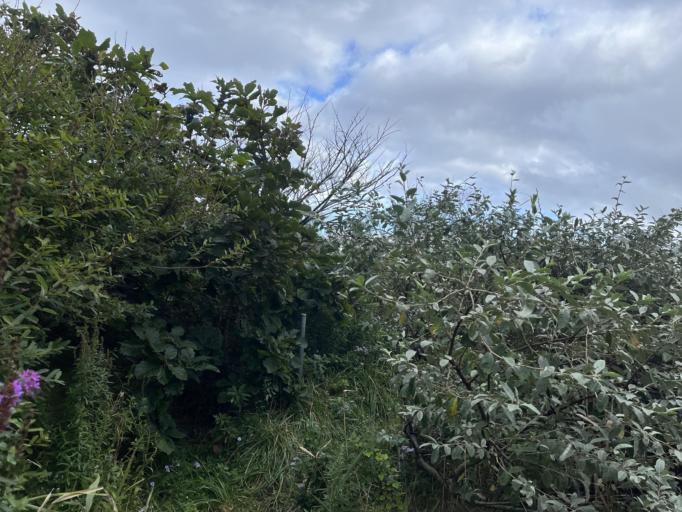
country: JP
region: Hokkaido
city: Muroran
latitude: 42.3308
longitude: 141.0199
